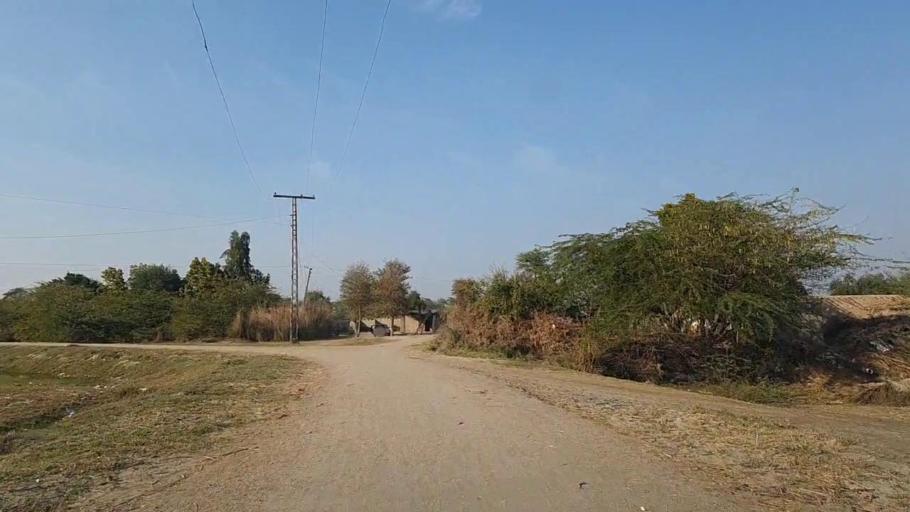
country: PK
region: Sindh
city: Nawabshah
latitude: 26.3835
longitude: 68.4852
